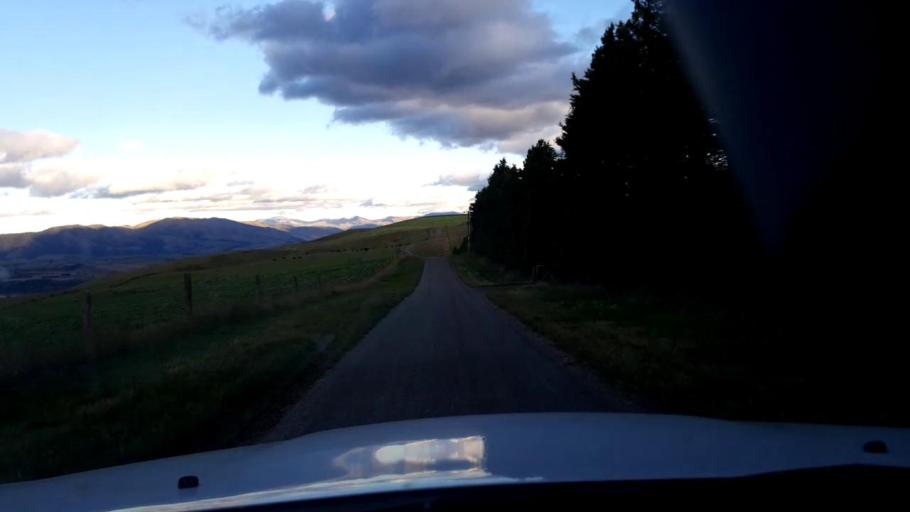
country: NZ
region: Canterbury
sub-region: Timaru District
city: Pleasant Point
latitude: -44.2568
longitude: 170.9138
